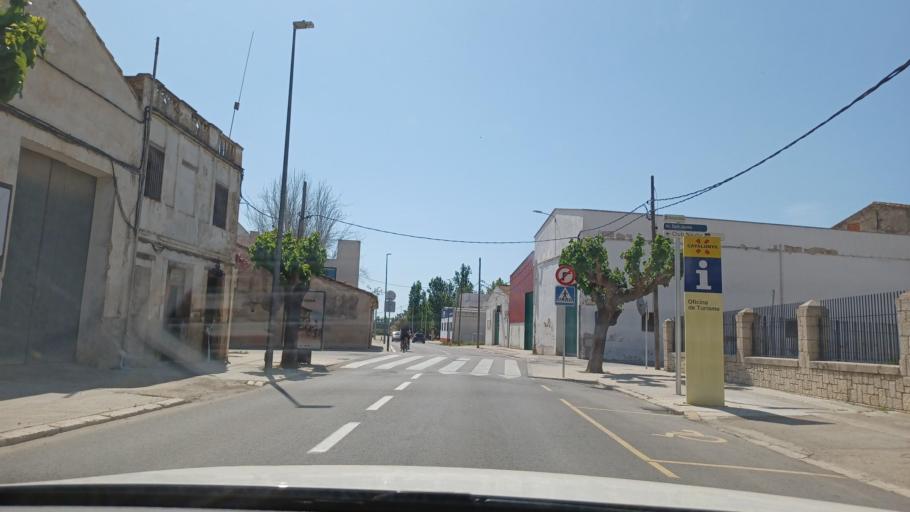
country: ES
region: Catalonia
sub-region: Provincia de Tarragona
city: Amposta
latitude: 40.7106
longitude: 0.5859
